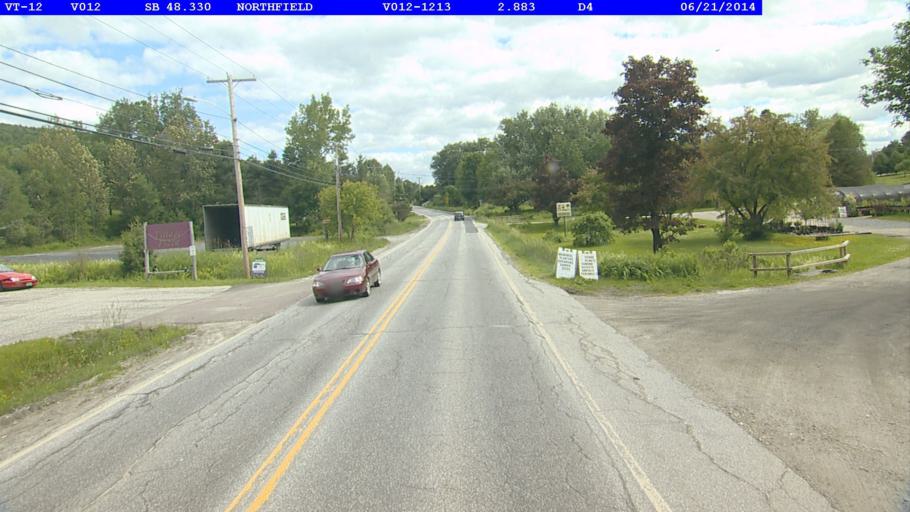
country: US
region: Vermont
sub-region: Washington County
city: Northfield
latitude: 44.1305
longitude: -72.6583
